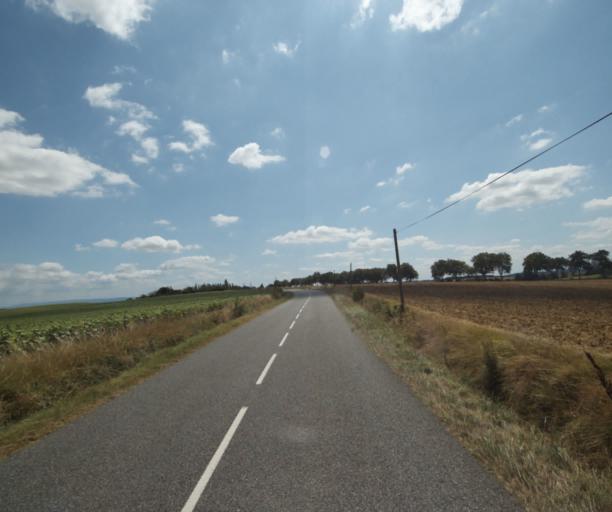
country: FR
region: Midi-Pyrenees
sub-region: Departement de la Haute-Garonne
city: Auriac-sur-Vendinelle
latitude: 43.4642
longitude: 1.8252
